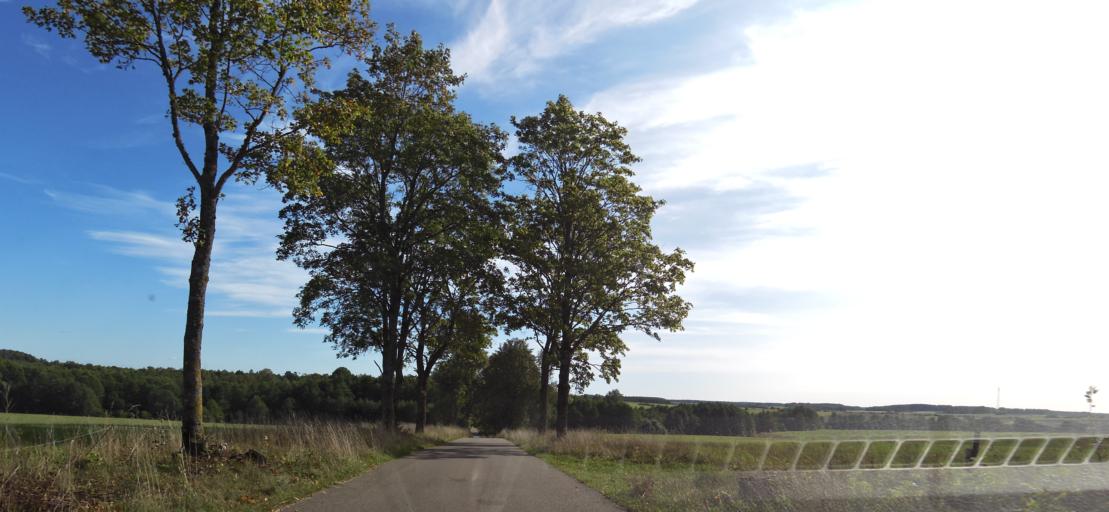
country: LT
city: Salcininkai
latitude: 54.4512
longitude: 25.5136
